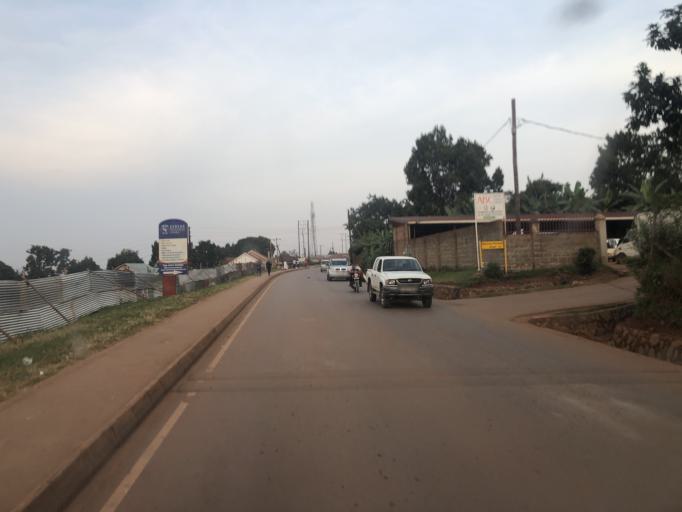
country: UG
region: Central Region
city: Kampala Central Division
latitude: 0.2924
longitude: 32.5332
